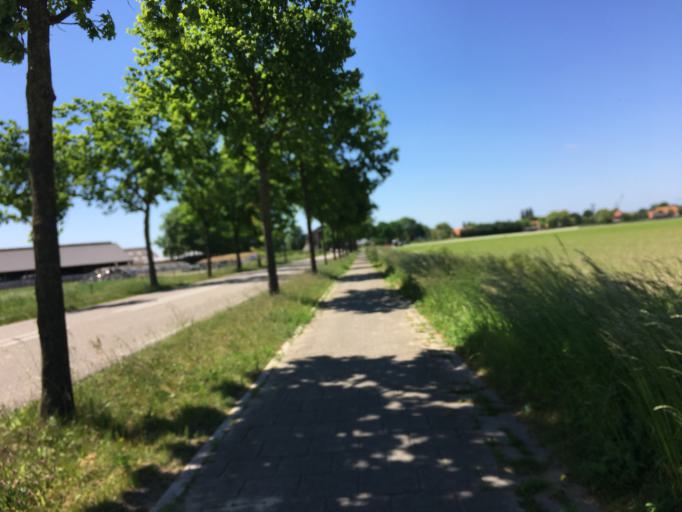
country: NL
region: North Brabant
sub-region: Gemeente Heusden
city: Heusden
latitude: 51.7303
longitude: 5.1666
